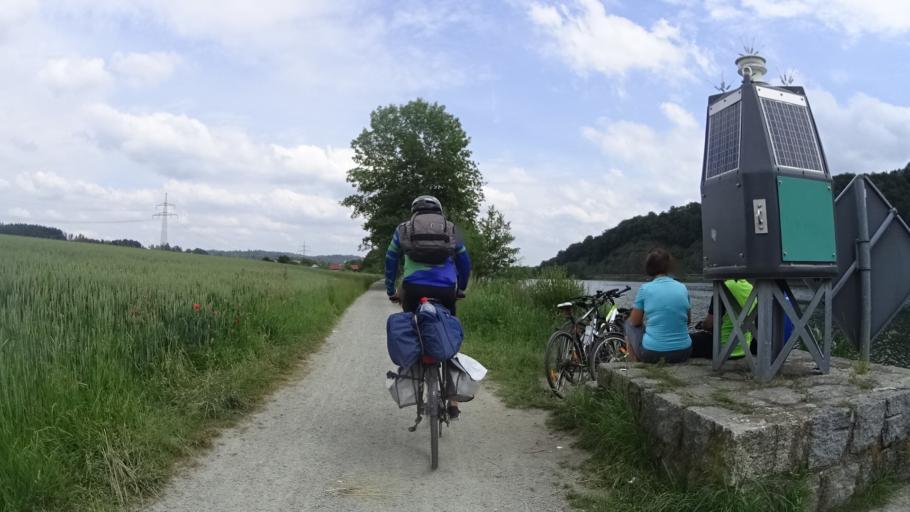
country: DE
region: Bavaria
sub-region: Lower Bavaria
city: Tiefenbach
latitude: 48.6021
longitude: 13.3403
